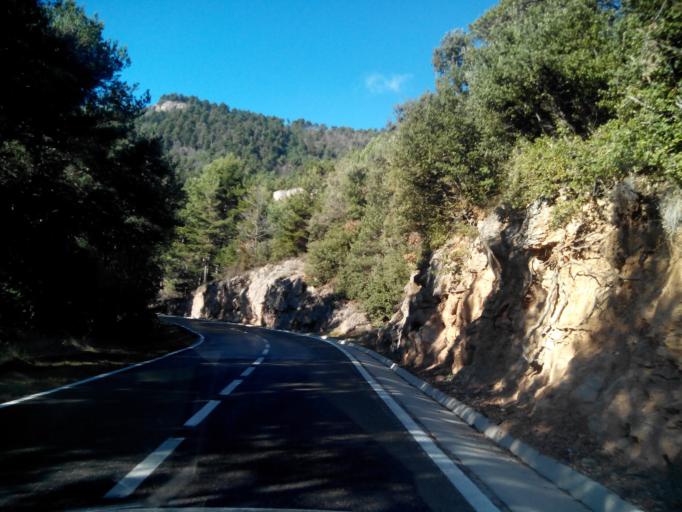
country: ES
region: Catalonia
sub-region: Provincia de Barcelona
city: Castellar del Riu
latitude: 42.0952
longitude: 1.7868
